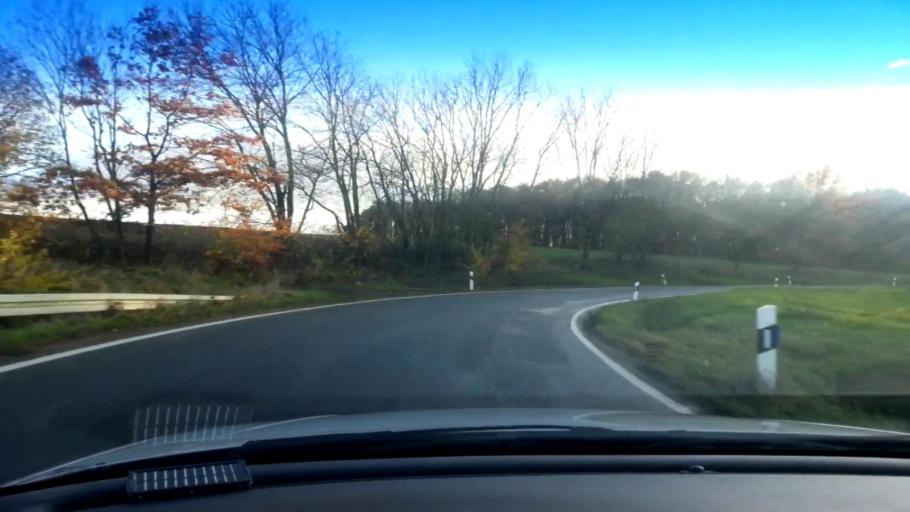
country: DE
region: Bavaria
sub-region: Upper Franconia
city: Hirschaid
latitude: 49.8476
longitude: 11.0214
